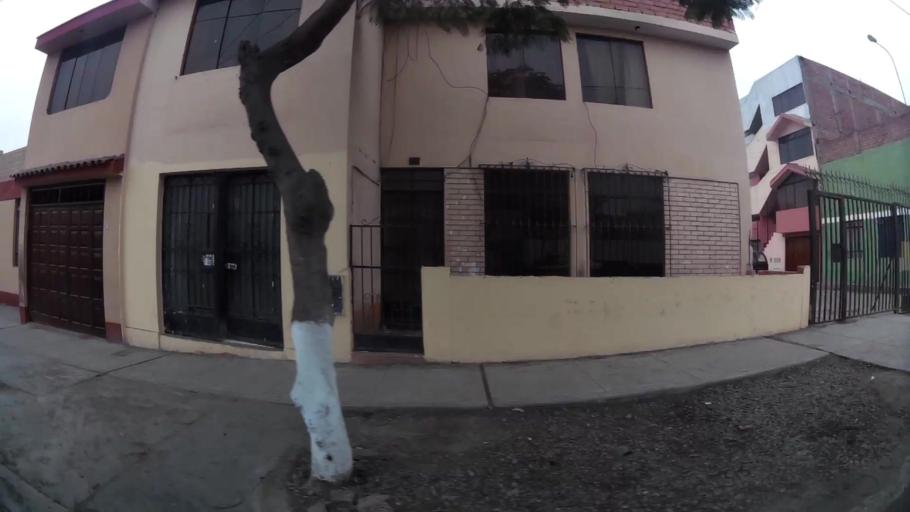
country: PE
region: Lima
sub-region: Lima
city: Surco
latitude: -12.1620
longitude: -76.9687
